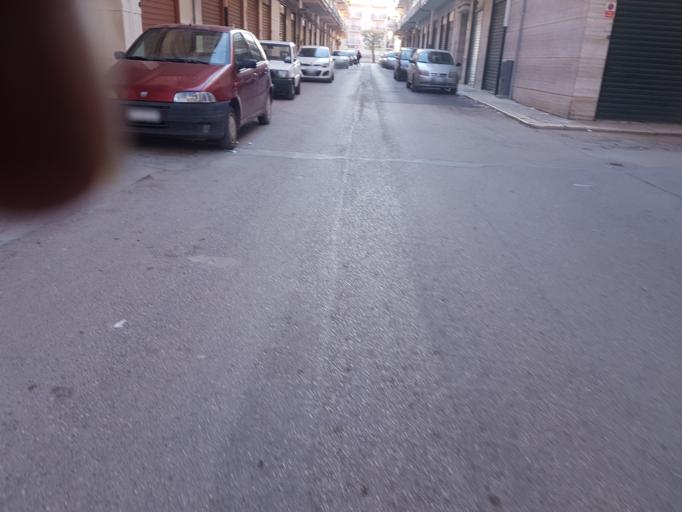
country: IT
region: Apulia
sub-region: Provincia di Bari
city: Corato
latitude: 41.1493
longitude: 16.4053
